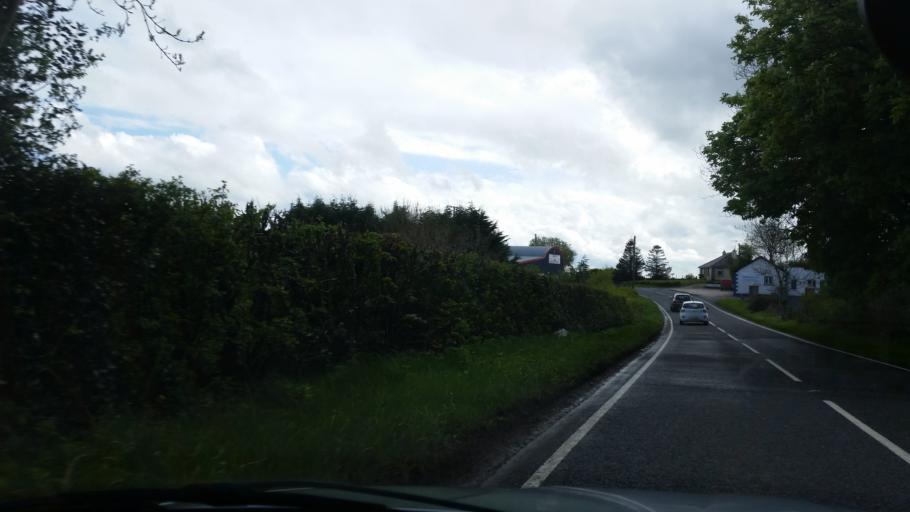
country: GB
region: Northern Ireland
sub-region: Omagh District
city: Omagh
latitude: 54.5559
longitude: -7.2818
